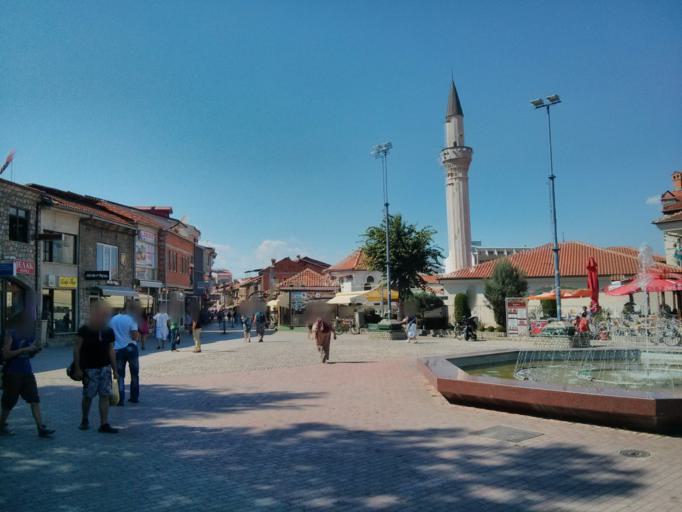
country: MK
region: Ohrid
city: Ohrid
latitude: 41.1160
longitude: 20.8004
